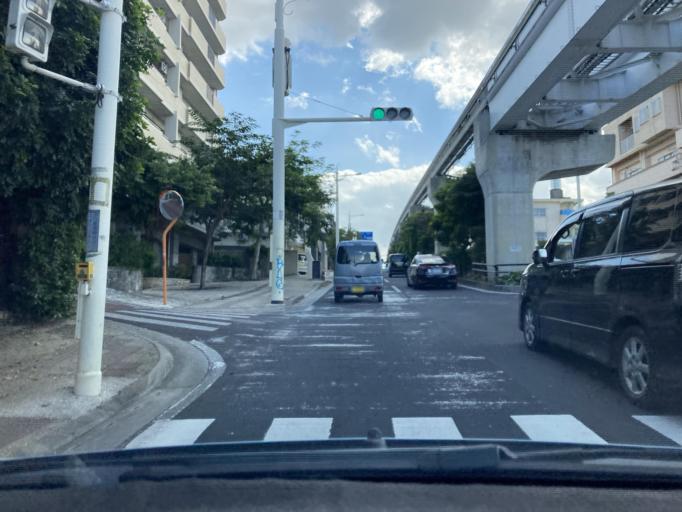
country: JP
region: Okinawa
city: Naha-shi
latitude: 26.2215
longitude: 127.7222
